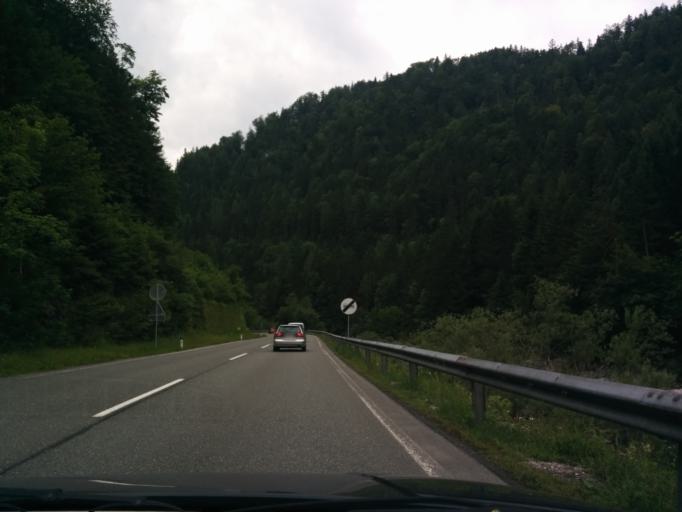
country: AT
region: Salzburg
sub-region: Politischer Bezirk Hallein
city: Abtenau
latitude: 47.5945
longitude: 13.2968
